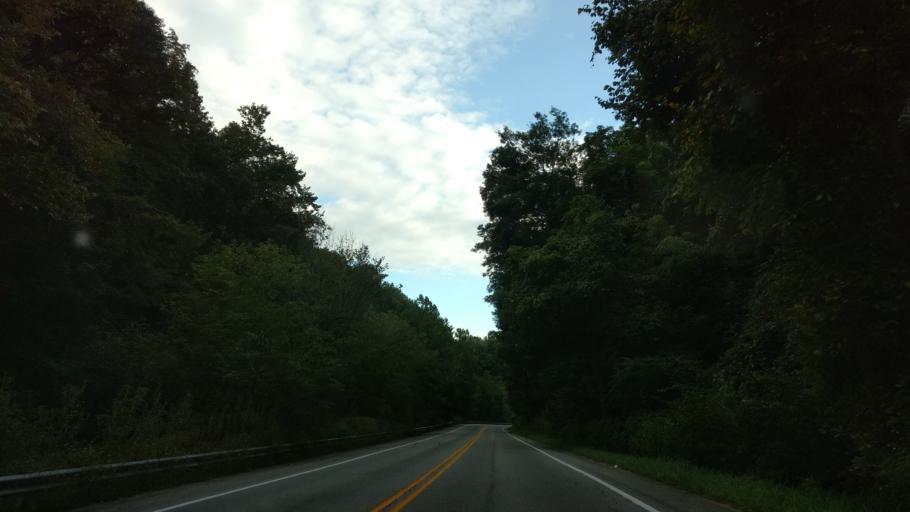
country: US
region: Pennsylvania
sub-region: Washington County
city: Speers
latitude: 40.1222
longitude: -79.8902
